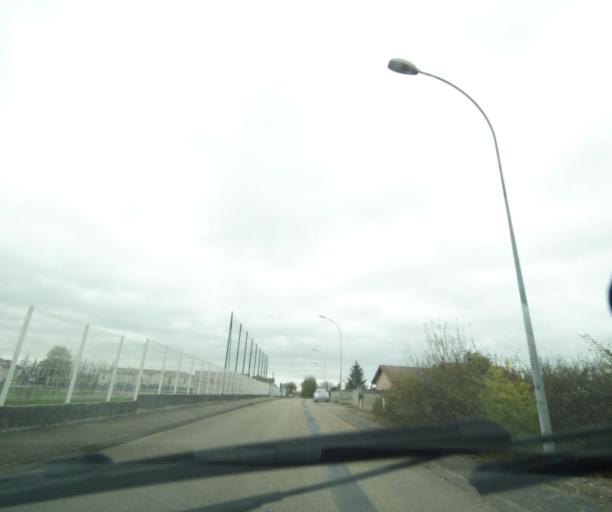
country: FR
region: Rhone-Alpes
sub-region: Departement de l'Ain
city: Loyettes
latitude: 45.7797
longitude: 5.2122
